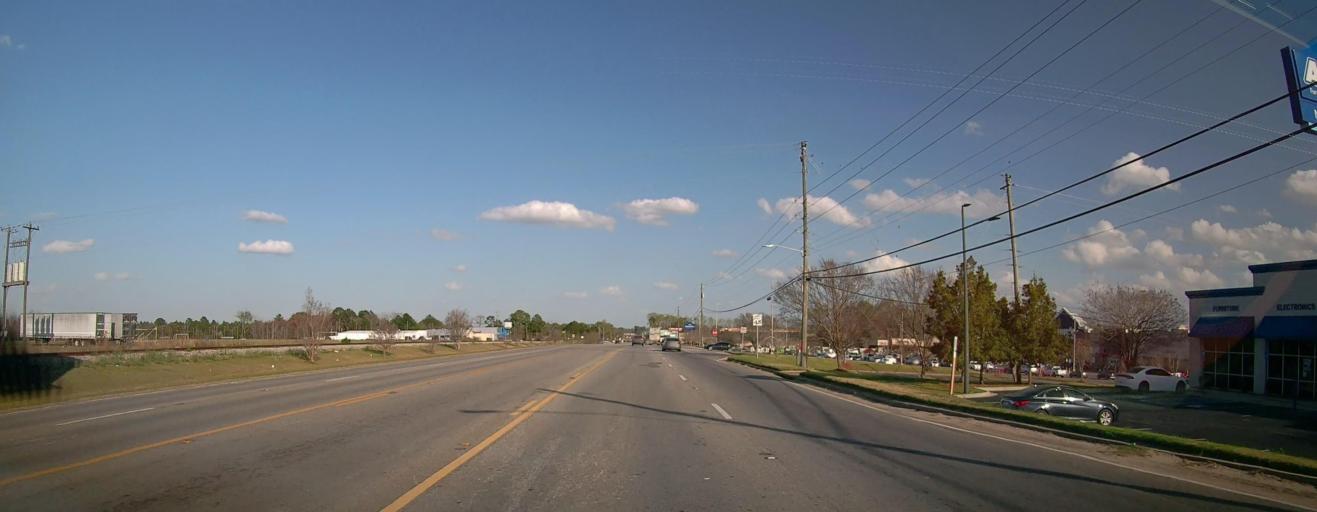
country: US
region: Georgia
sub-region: Toombs County
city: Lyons
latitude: 32.2045
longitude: -82.3597
